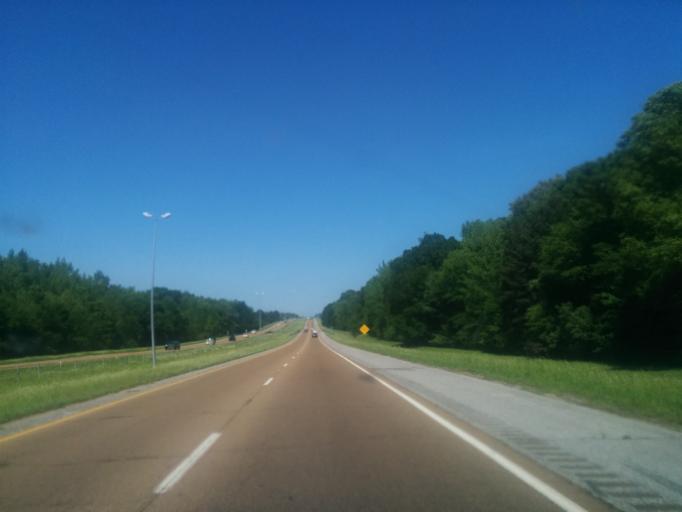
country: US
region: Mississippi
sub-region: Hinds County
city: Jackson
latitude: 32.3788
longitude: -90.2076
